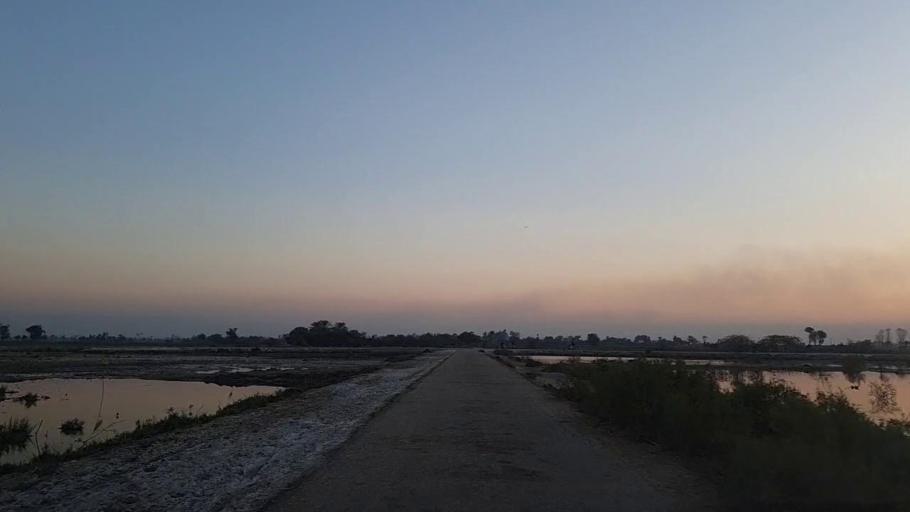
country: PK
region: Sindh
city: Bandhi
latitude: 26.5897
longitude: 68.3359
